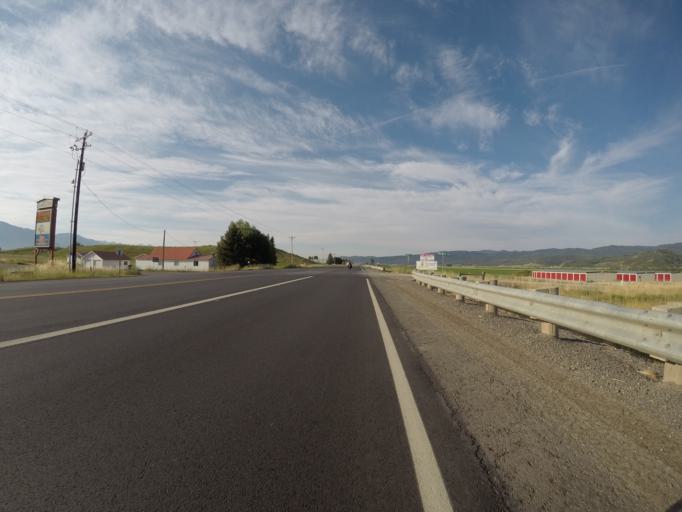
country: US
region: Wyoming
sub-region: Lincoln County
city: Afton
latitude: 42.9683
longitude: -111.0125
